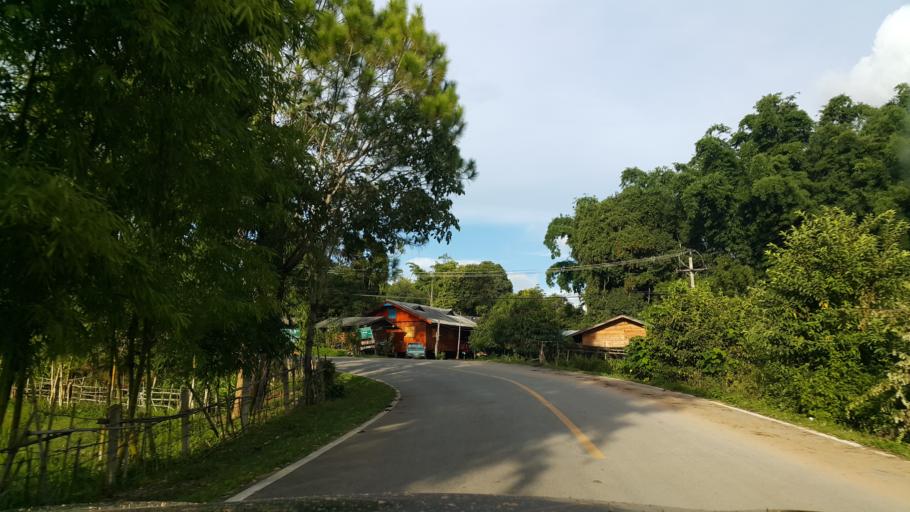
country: TH
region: Chiang Mai
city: Chaem Luang
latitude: 19.0799
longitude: 98.3361
